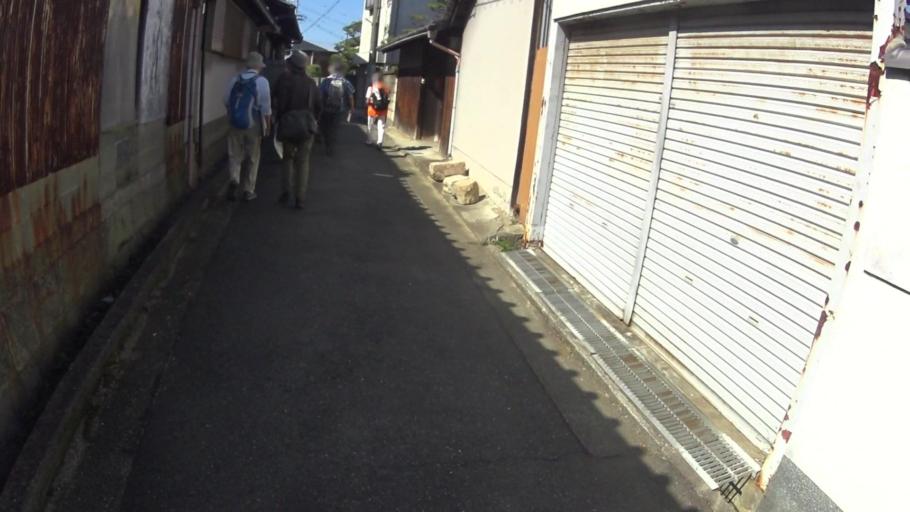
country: JP
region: Osaka
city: Sakai
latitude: 34.5442
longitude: 135.4730
